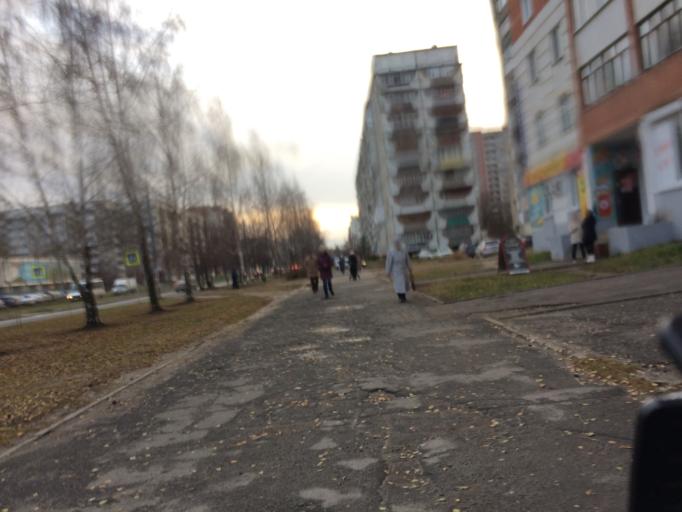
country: RU
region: Mariy-El
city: Yoshkar-Ola
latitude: 56.6335
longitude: 47.9194
